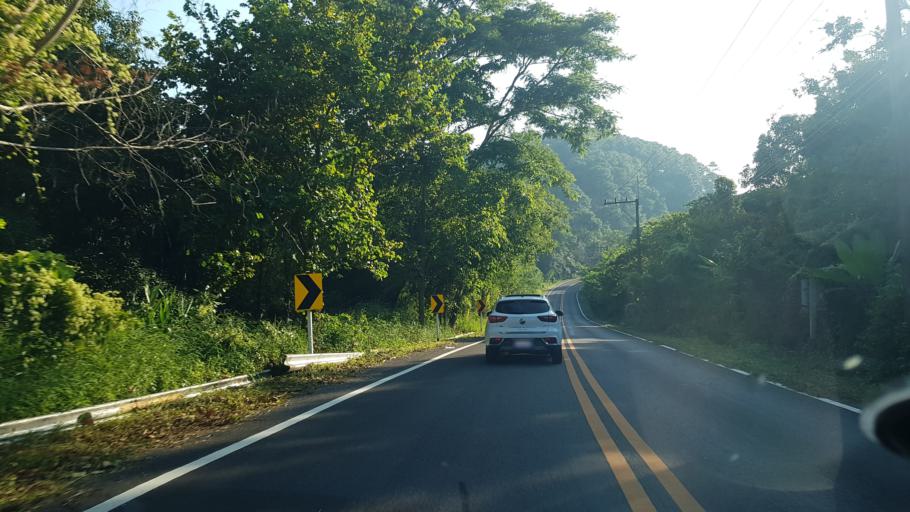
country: TH
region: Chiang Rai
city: Mae Fa Luang
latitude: 20.3100
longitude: 99.8195
